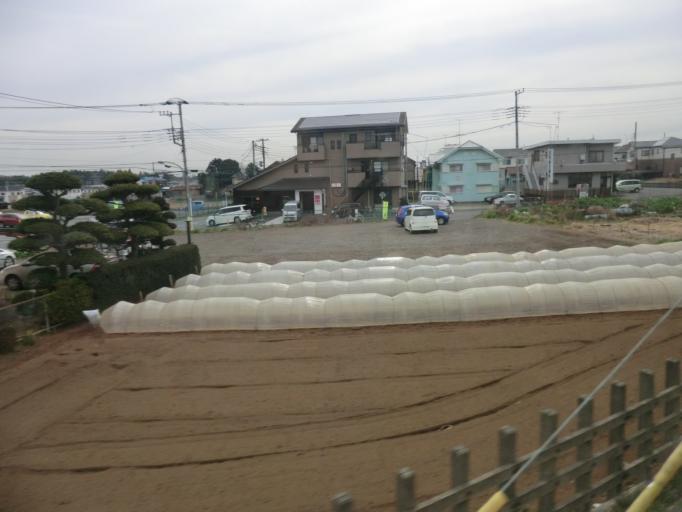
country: JP
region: Chiba
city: Kashiwa
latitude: 35.8072
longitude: 139.9990
